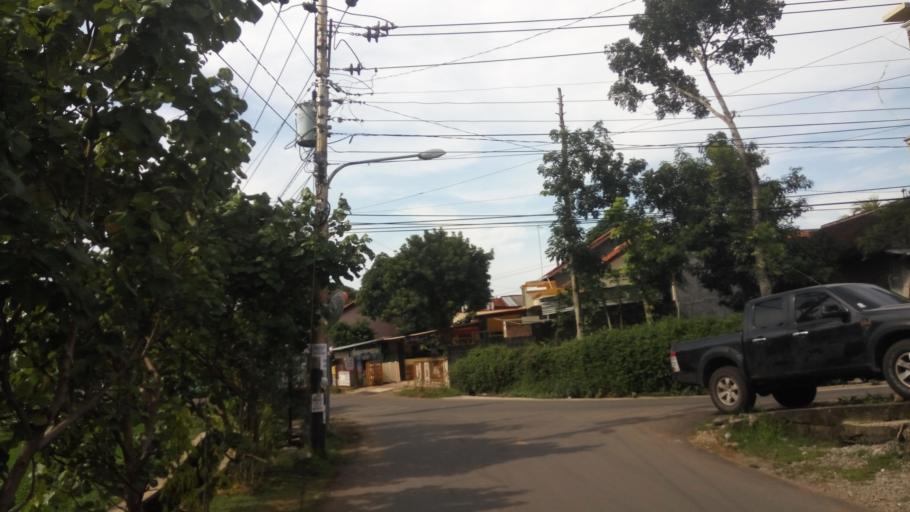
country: ID
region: Central Java
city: Ungaran
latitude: -7.1332
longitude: 110.4206
